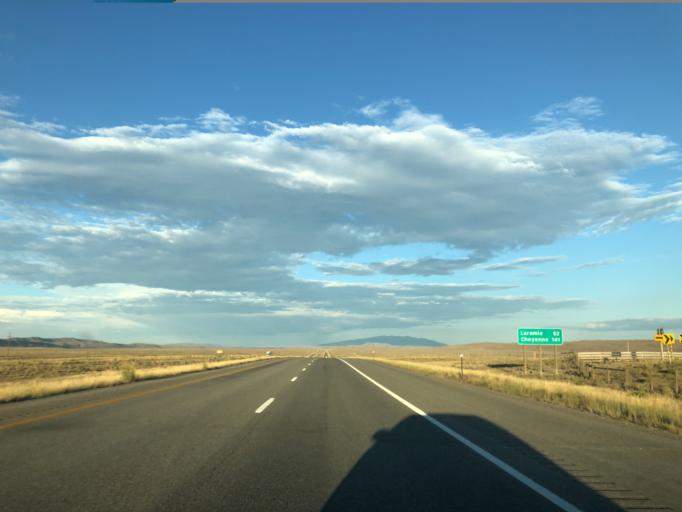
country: US
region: Wyoming
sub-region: Carbon County
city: Rawlins
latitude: 41.7708
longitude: -107.0570
